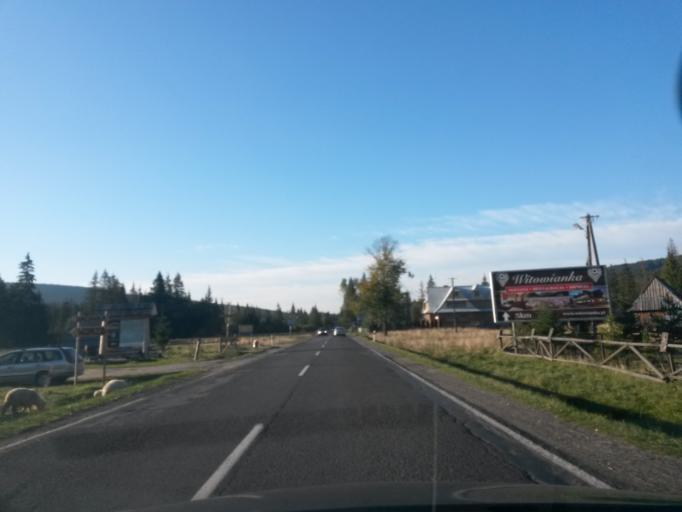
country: PL
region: Lesser Poland Voivodeship
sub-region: Powiat tatrzanski
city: Koscielisko
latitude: 49.2846
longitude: 19.8549
